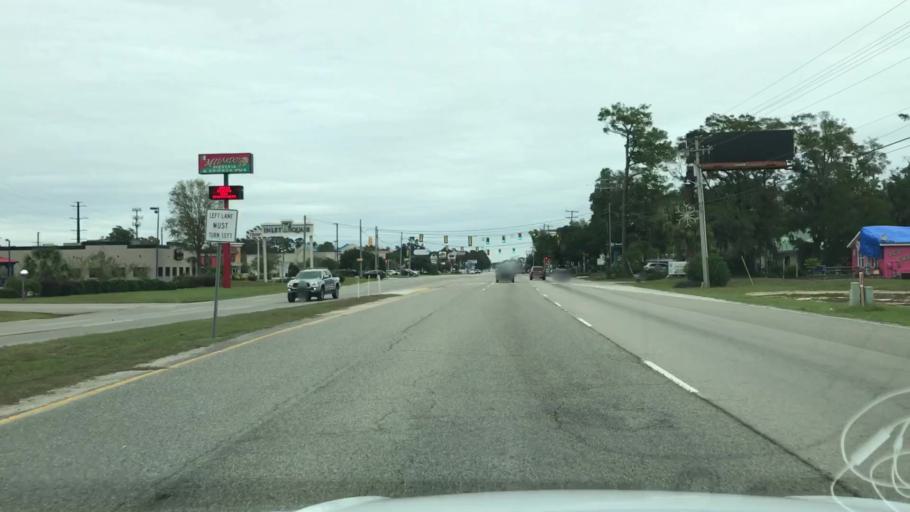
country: US
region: South Carolina
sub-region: Horry County
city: Garden City
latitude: 33.5780
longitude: -79.0234
